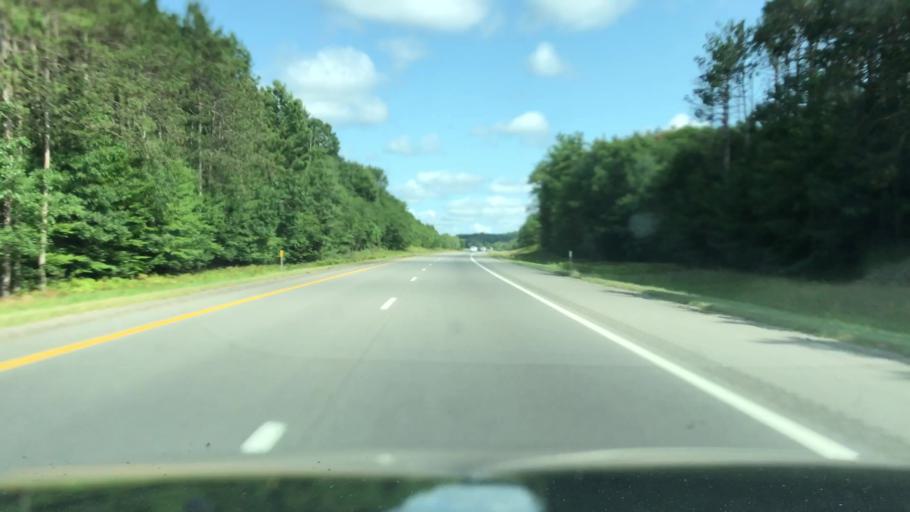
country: US
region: Michigan
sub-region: Mecosta County
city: Big Rapids
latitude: 43.6144
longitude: -85.4959
